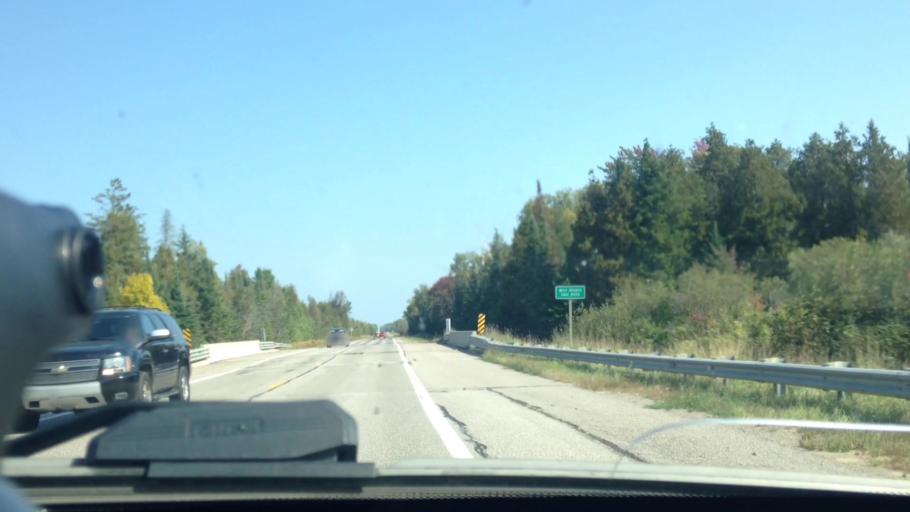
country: US
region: Michigan
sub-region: Luce County
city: Newberry
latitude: 46.3035
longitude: -85.3943
